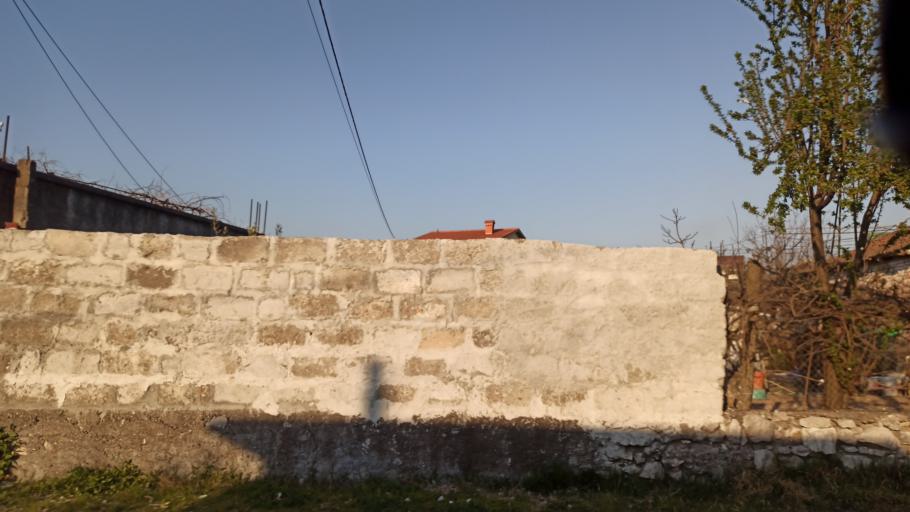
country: AL
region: Shkoder
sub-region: Rrethi i Shkodres
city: Shkoder
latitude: 42.0783
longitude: 19.5013
